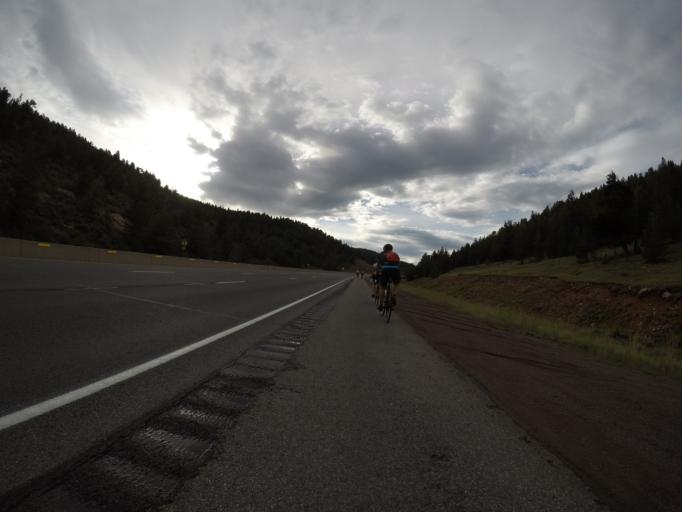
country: US
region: Wyoming
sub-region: Albany County
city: Laramie
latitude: 41.2620
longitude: -105.4611
